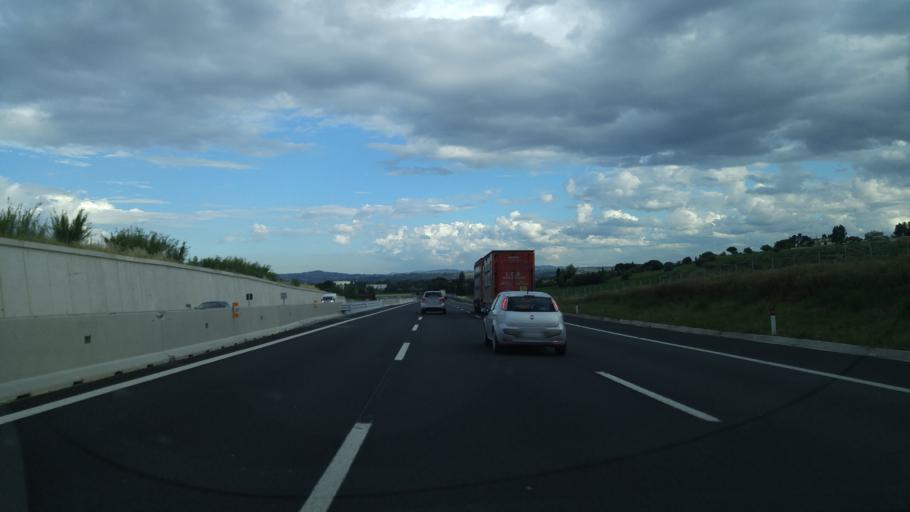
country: IT
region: Emilia-Romagna
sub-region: Provincia di Rimini
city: Riccione
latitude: 43.9747
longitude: 12.6627
